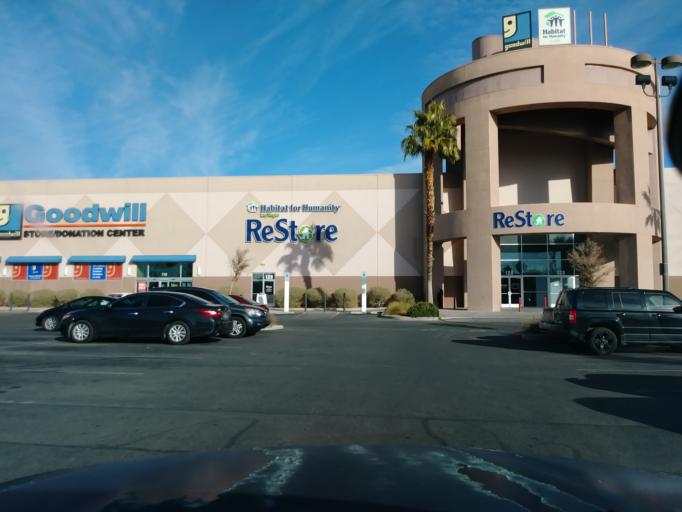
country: US
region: Nevada
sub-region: Clark County
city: Spring Valley
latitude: 36.1450
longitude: -115.2033
